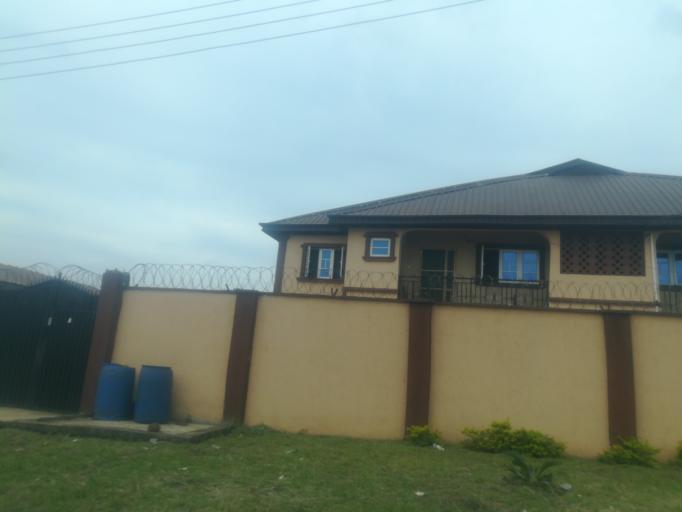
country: NG
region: Oyo
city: Ibadan
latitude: 7.3746
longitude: 3.9709
